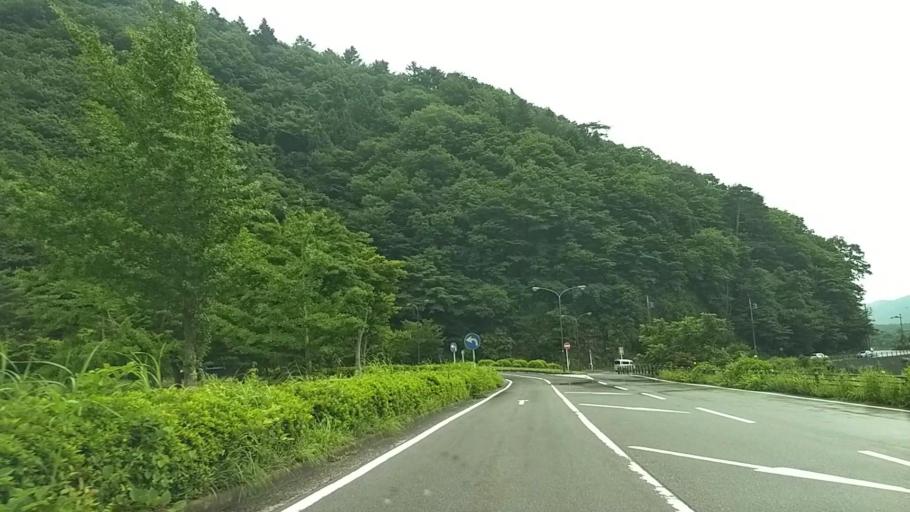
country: JP
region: Yamanashi
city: Fujikawaguchiko
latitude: 35.4939
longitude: 138.6106
